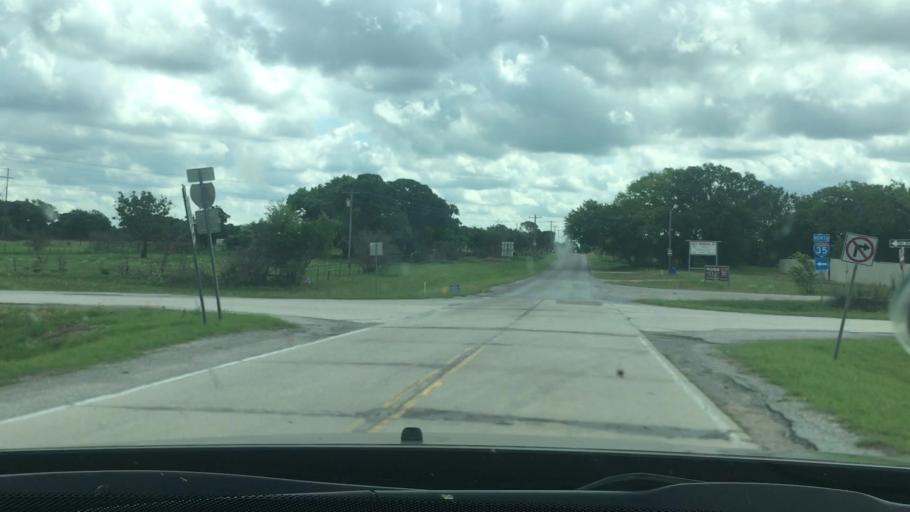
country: US
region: Oklahoma
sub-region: Love County
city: Marietta
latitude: 33.7951
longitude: -97.1331
